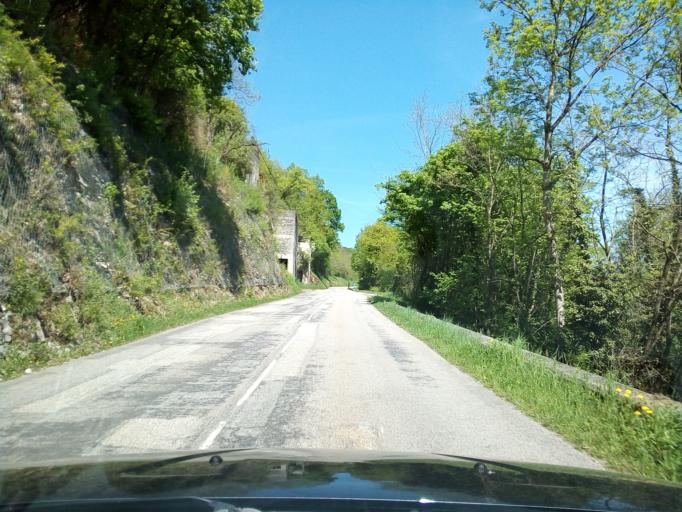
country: FR
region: Rhone-Alpes
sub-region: Departement de l'Isere
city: Chapareillan
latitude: 45.4712
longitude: 5.9777
